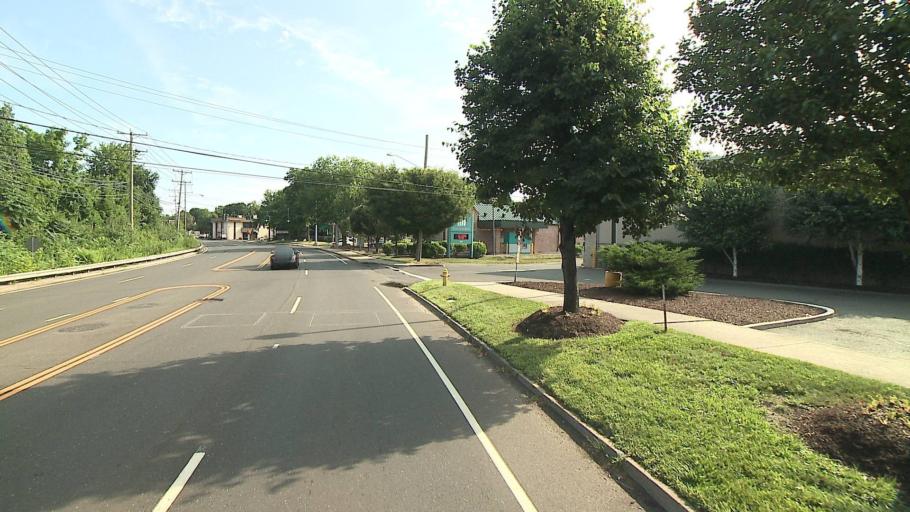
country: US
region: Connecticut
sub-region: Fairfield County
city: Wilton
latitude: 41.1594
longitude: -73.4194
